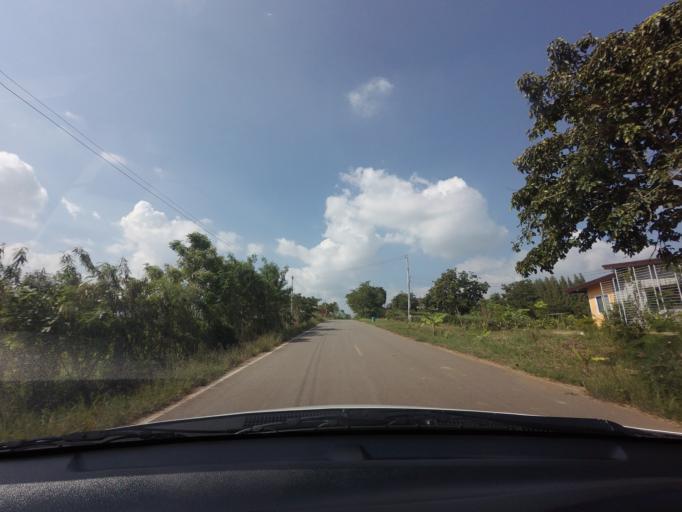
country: TH
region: Nakhon Ratchasima
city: Wang Nam Khiao
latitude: 14.4880
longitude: 101.6269
